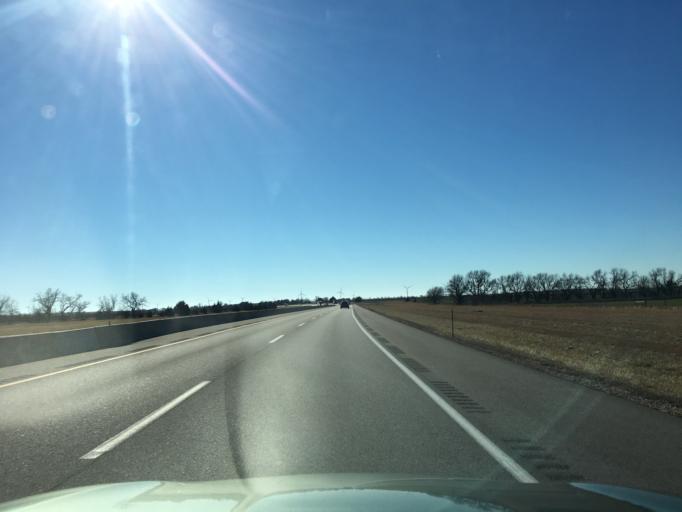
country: US
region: Kansas
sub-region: Sumner County
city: Wellington
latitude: 37.1978
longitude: -97.3404
